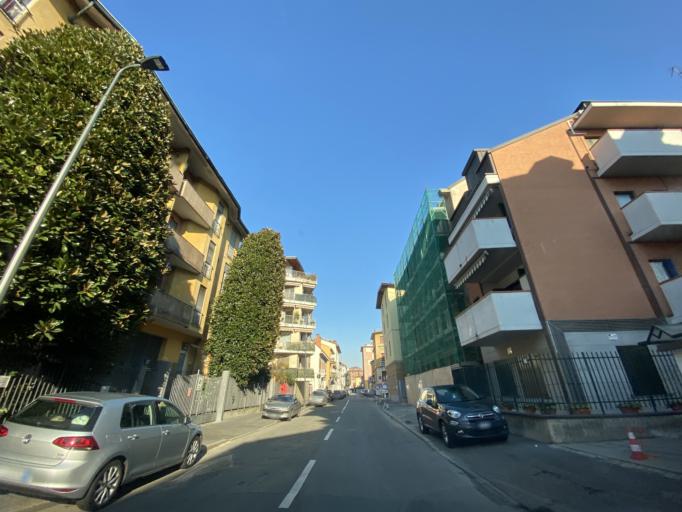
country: IT
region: Lombardy
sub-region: Citta metropolitana di Milano
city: Bresso
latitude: 45.5052
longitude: 9.2066
